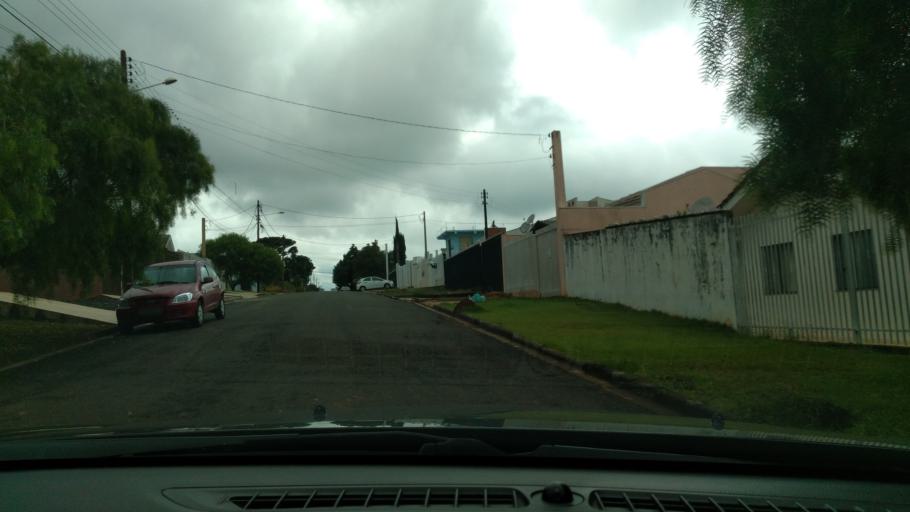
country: BR
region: Parana
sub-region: Guarapuava
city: Guarapuava
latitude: -25.3942
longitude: -51.4927
